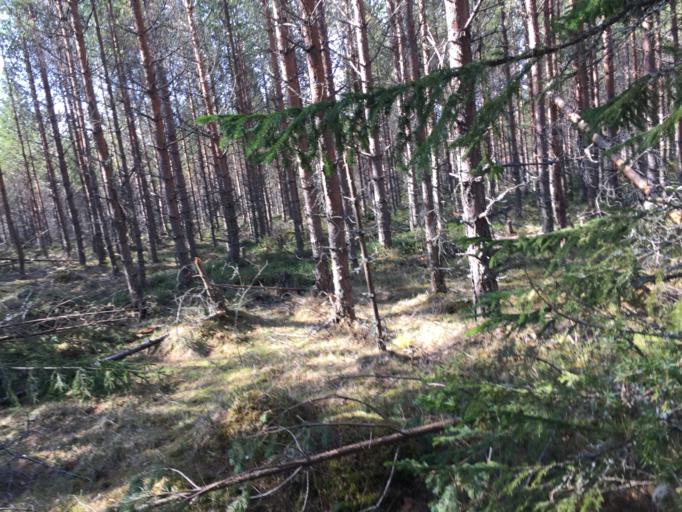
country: SE
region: Dalarna
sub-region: Faluns Kommun
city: Bjursas
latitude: 60.8413
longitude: 15.3273
